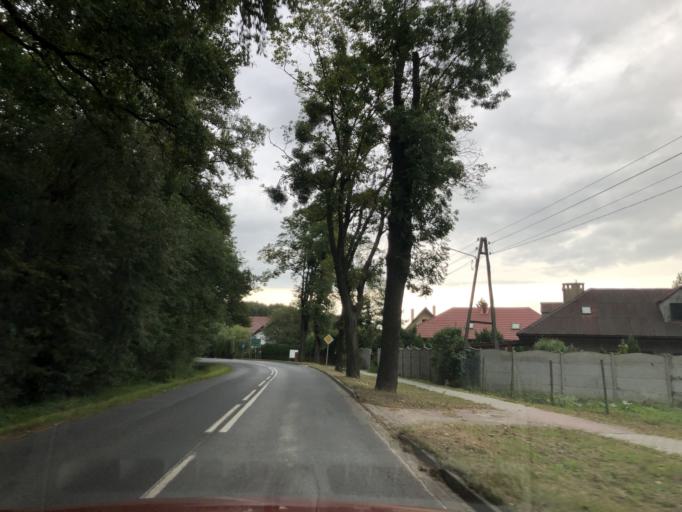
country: PL
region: Lower Silesian Voivodeship
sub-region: Powiat wroclawski
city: Dlugoleka
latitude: 51.1849
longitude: 17.1869
